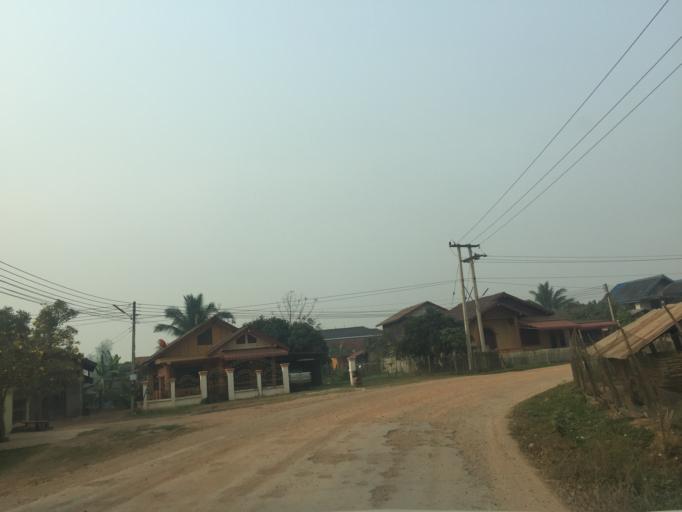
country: LA
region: Xiagnabouli
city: Sainyabuli
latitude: 19.2585
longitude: 101.6977
